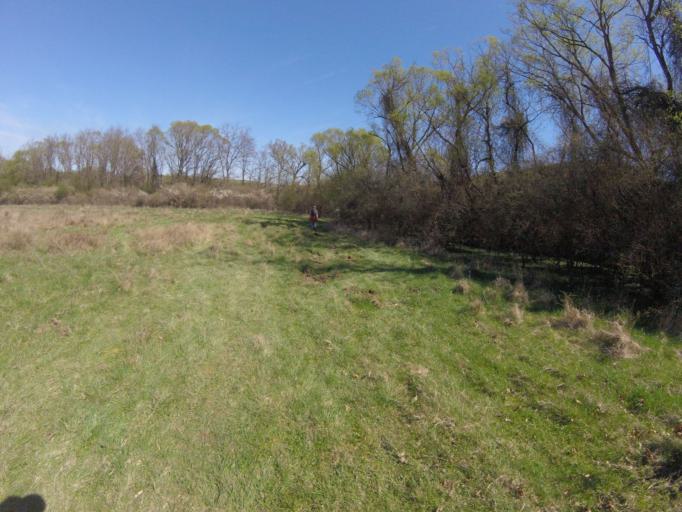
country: HU
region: Borsod-Abauj-Zemplen
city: Szendro
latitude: 48.4116
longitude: 20.7770
